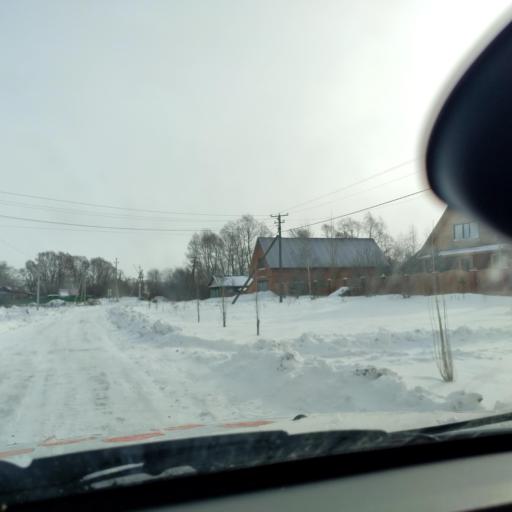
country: RU
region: Bashkortostan
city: Mikhaylovka
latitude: 54.8714
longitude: 55.7482
